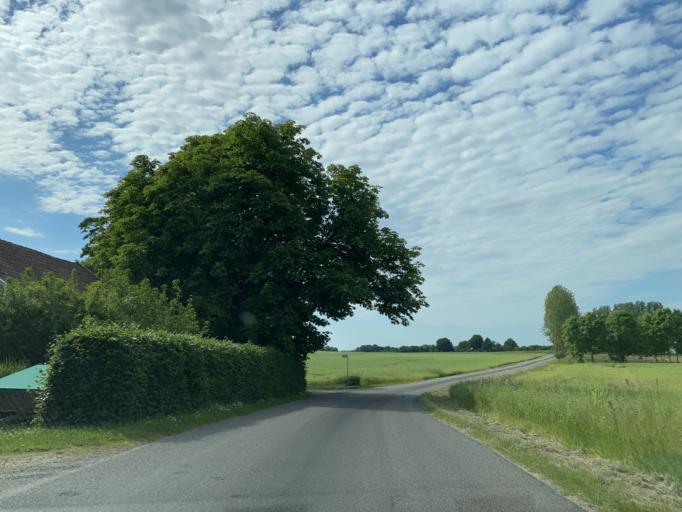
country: DK
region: Central Jutland
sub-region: Skanderborg Kommune
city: Galten
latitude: 56.2082
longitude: 9.9039
